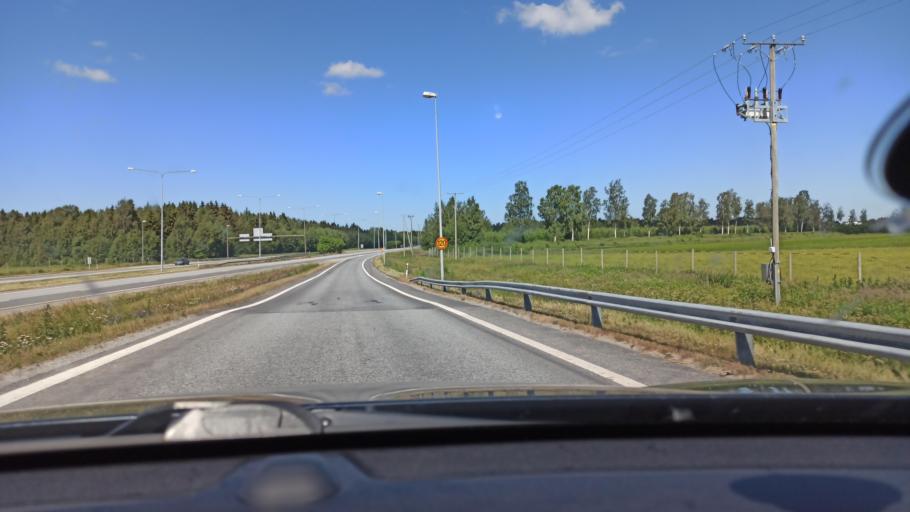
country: FI
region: Ostrobothnia
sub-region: Vaasa
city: Ristinummi
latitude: 63.0358
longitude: 21.7403
